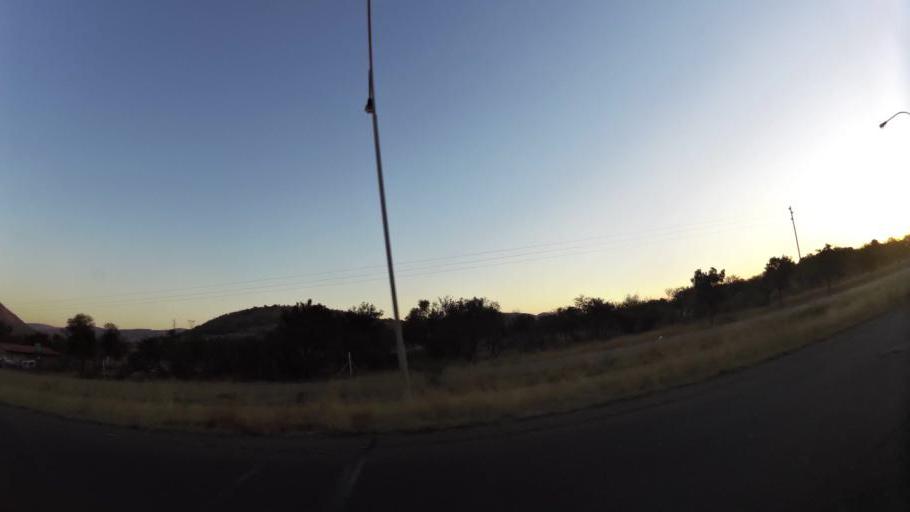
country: ZA
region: North-West
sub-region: Bojanala Platinum District Municipality
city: Rustenburg
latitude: -25.6216
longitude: 27.1829
